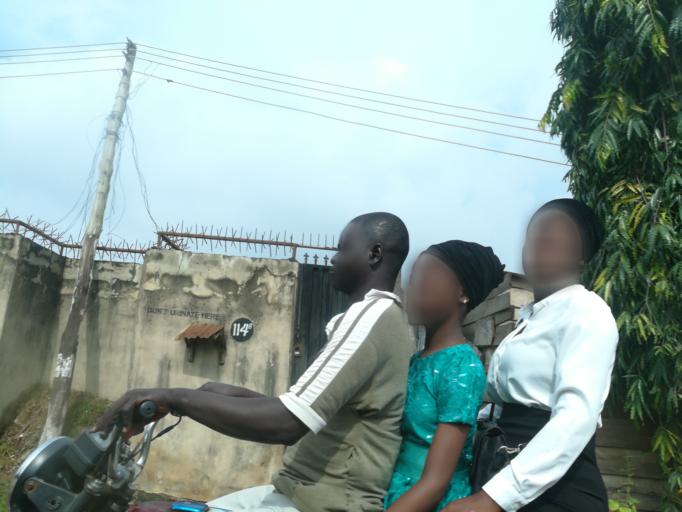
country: NG
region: Lagos
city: Agege
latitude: 6.5960
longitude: 3.3033
